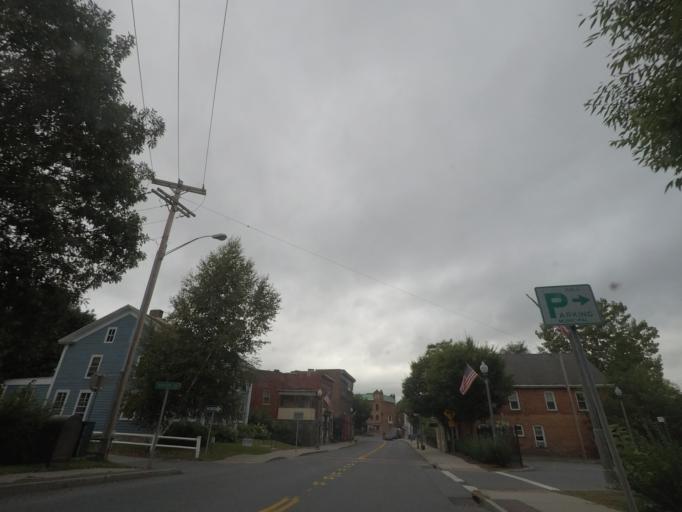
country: US
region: New York
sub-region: Rensselaer County
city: Hoosick Falls
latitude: 42.9021
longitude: -73.3493
